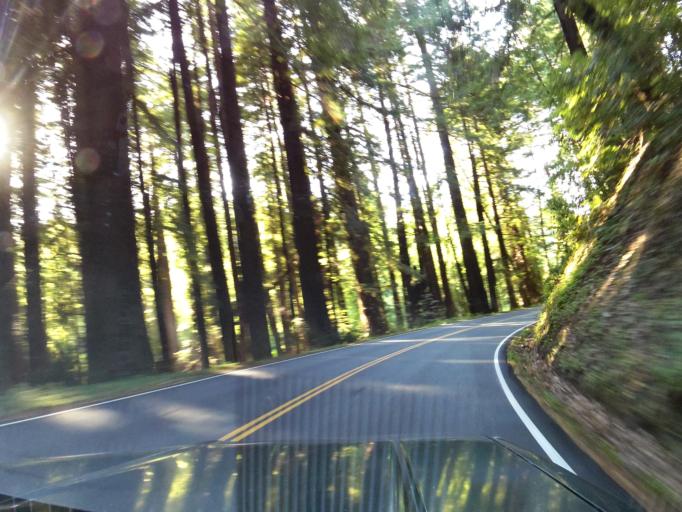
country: US
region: California
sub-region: Mendocino County
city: Boonville
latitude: 39.1572
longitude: -123.6373
